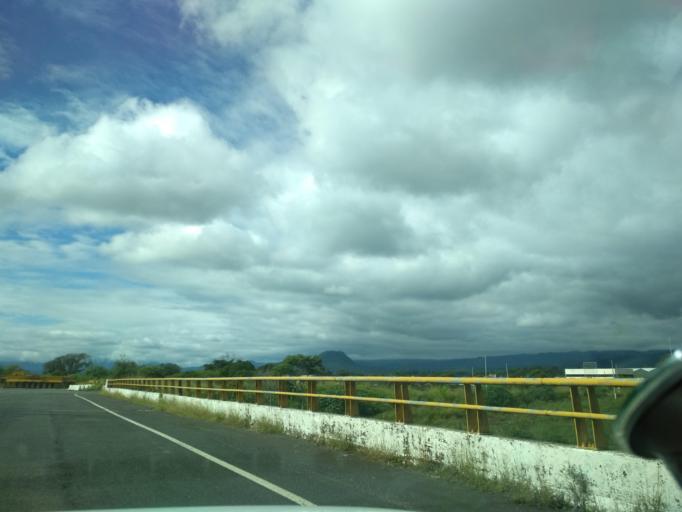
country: MX
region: Veracruz
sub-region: Coatepec
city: Las Lomas
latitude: 19.4465
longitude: -96.9305
